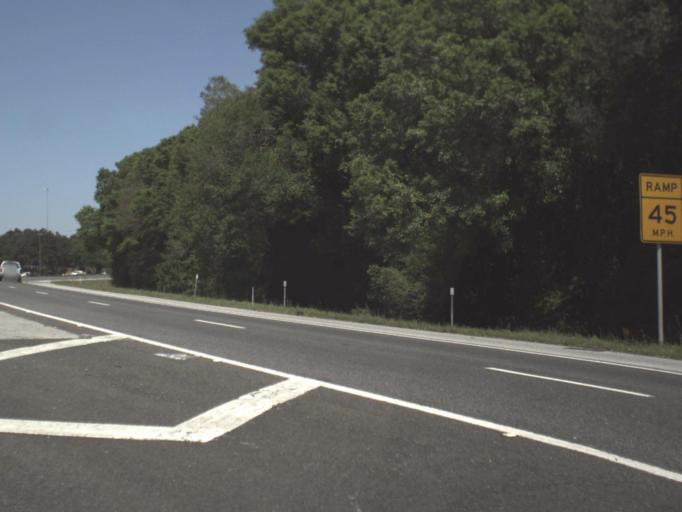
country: US
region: Florida
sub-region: Escambia County
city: Ensley
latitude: 30.5045
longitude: -87.2648
